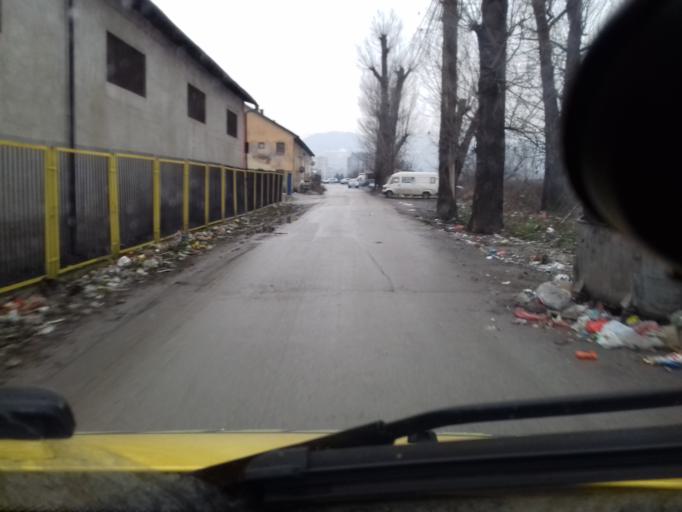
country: BA
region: Federation of Bosnia and Herzegovina
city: Zenica
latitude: 44.2205
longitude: 17.9093
